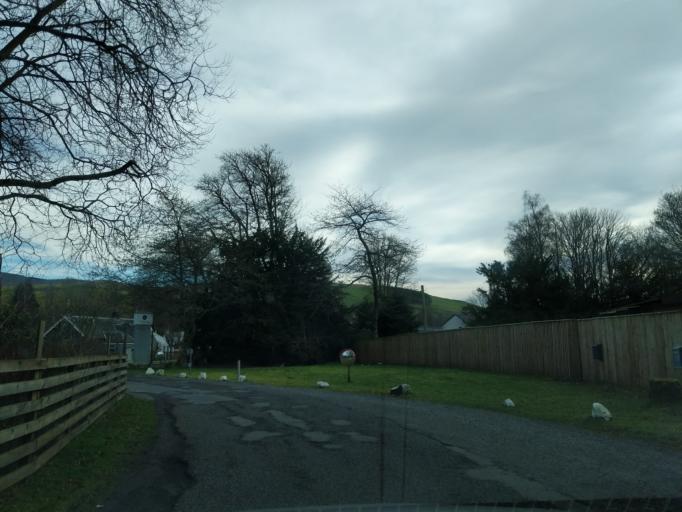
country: GB
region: Scotland
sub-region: The Scottish Borders
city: Peebles
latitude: 55.7123
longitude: -3.2095
